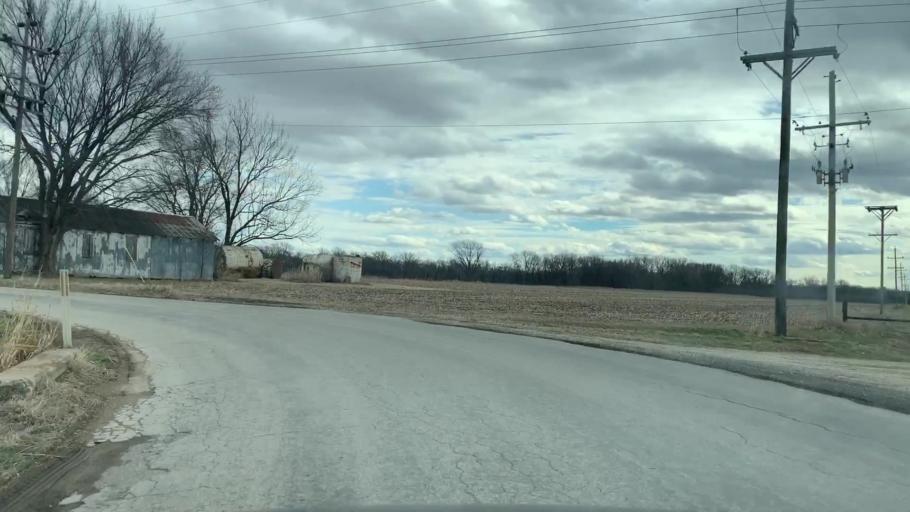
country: US
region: Kansas
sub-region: Allen County
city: Humboldt
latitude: 37.8111
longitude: -95.4524
